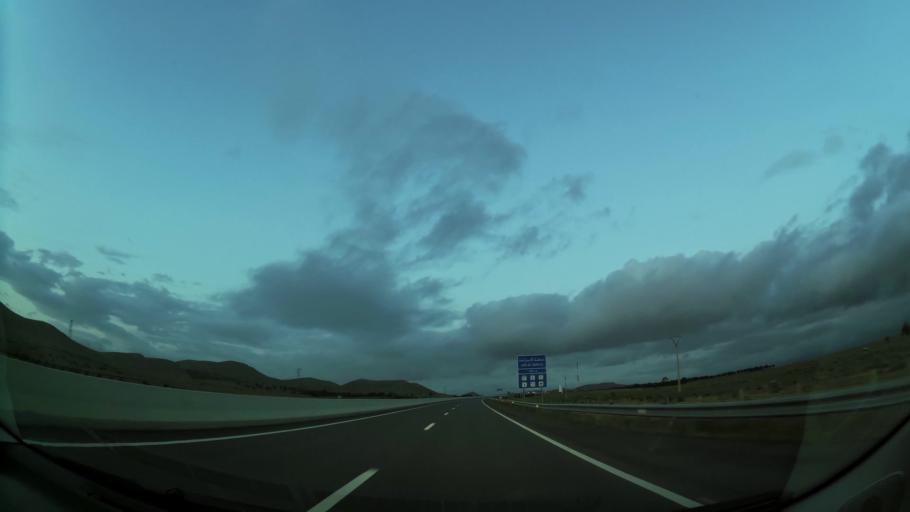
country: MA
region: Oriental
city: El Aioun
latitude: 34.6173
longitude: -2.4499
